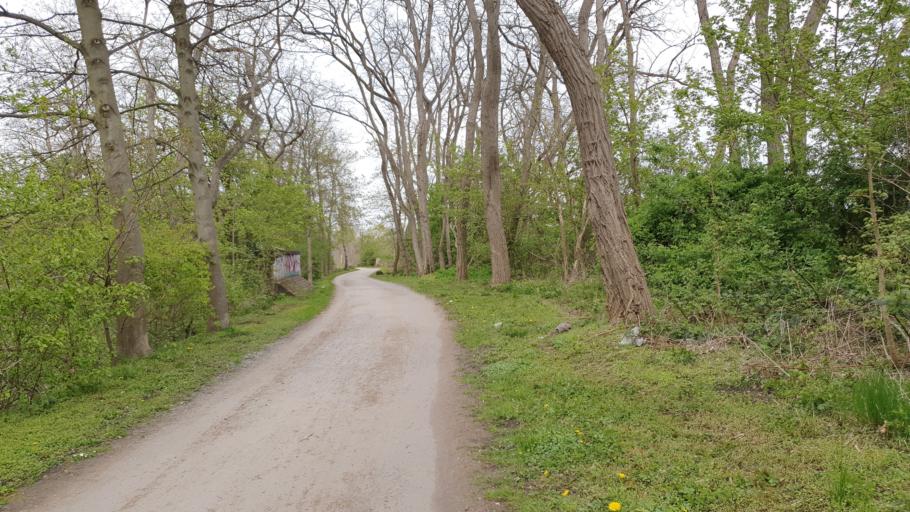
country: DE
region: North Rhine-Westphalia
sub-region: Regierungsbezirk Dusseldorf
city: Oberhausen
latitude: 51.5009
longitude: 6.8455
